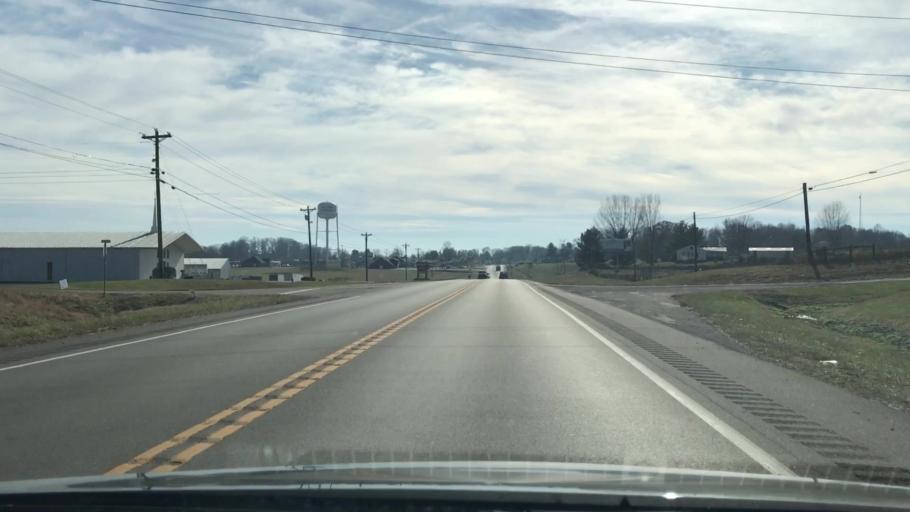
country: US
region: Kentucky
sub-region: Monroe County
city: Tompkinsville
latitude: 36.7307
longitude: -85.6876
